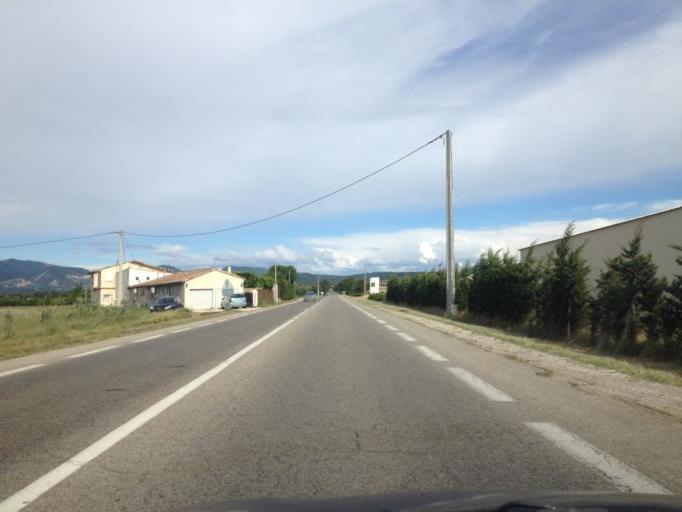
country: FR
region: Provence-Alpes-Cote d'Azur
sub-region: Departement du Vaucluse
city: Valreas
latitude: 44.3886
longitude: 4.9732
